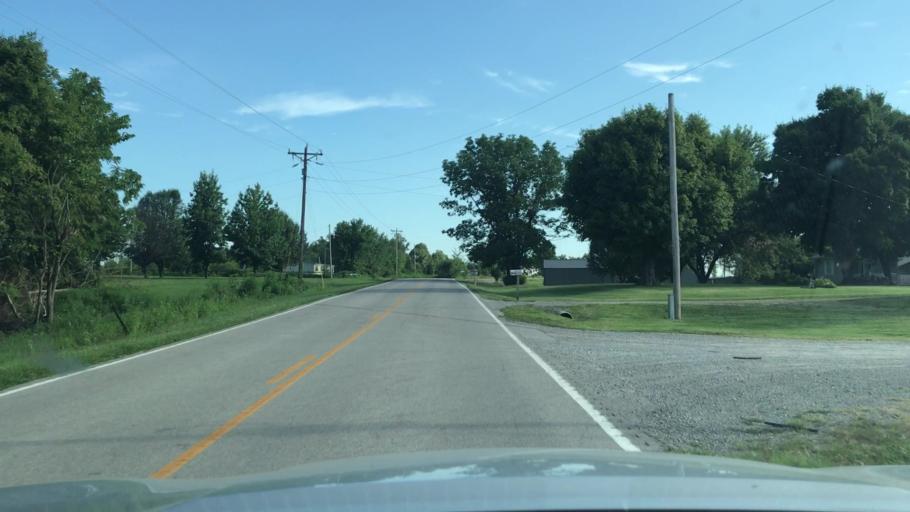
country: US
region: Kentucky
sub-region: Todd County
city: Elkton
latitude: 36.9287
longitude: -87.1622
